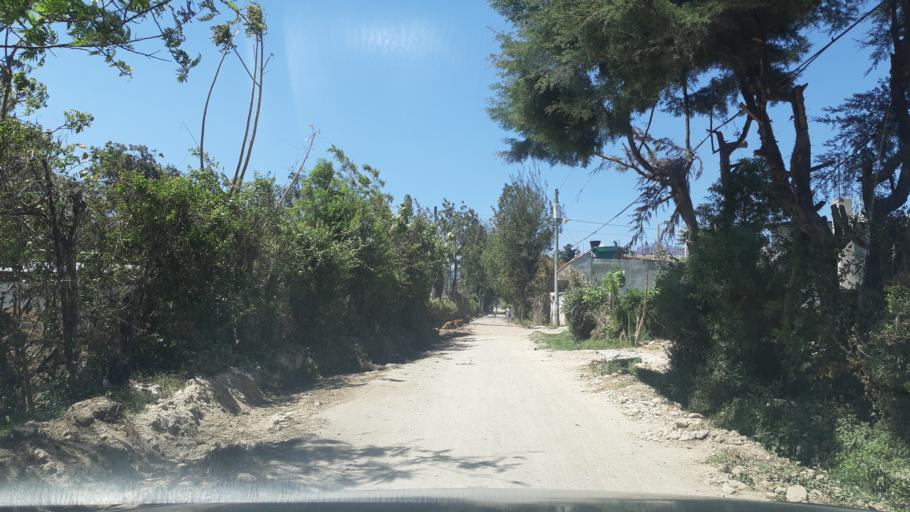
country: GT
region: Chimaltenango
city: El Tejar
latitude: 14.6494
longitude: -90.8059
